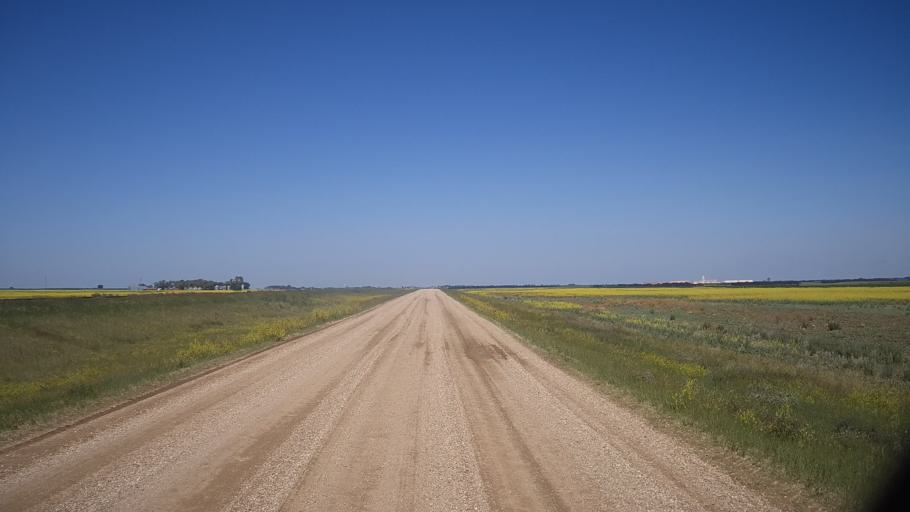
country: CA
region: Saskatchewan
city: Watrous
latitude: 51.8650
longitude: -105.9760
